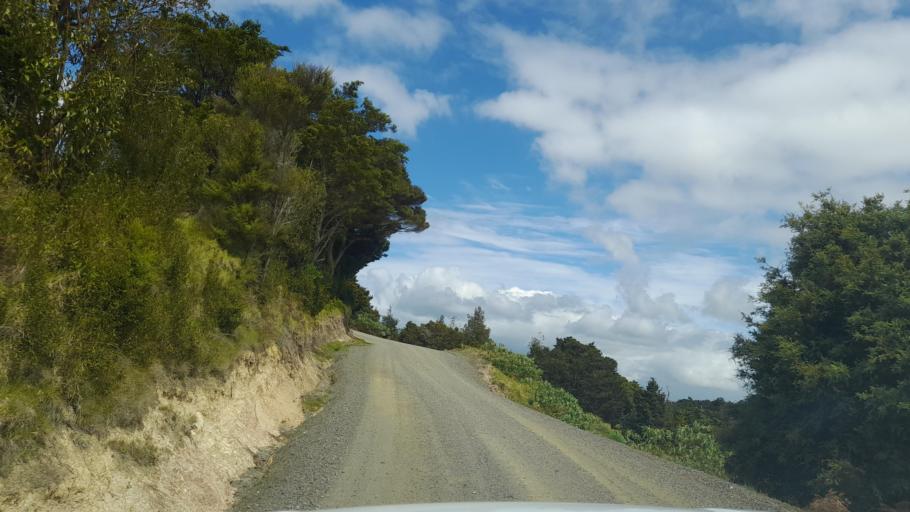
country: NZ
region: Auckland
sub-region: Auckland
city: Wellsford
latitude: -36.2078
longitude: 174.3351
